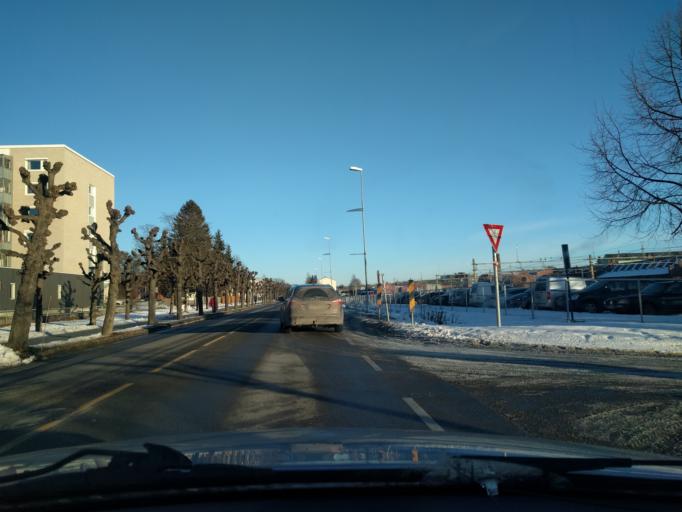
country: NO
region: Hedmark
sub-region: Hamar
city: Hamar
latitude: 60.7914
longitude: 11.0826
